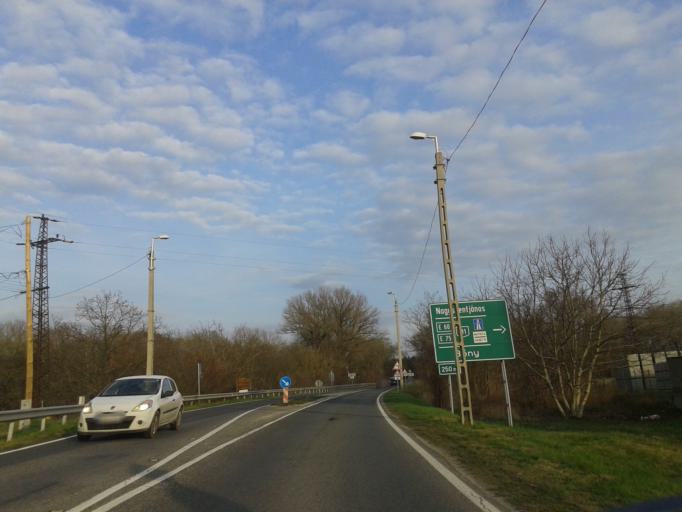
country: HU
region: Gyor-Moson-Sopron
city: Bony
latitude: 47.7330
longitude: 17.8435
